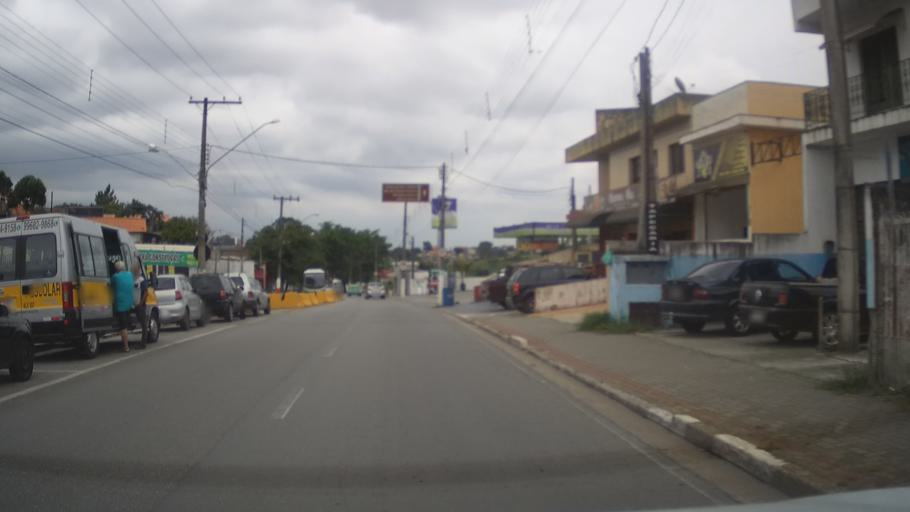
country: BR
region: Sao Paulo
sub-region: Aruja
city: Aruja
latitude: -23.3881
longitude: -46.3137
